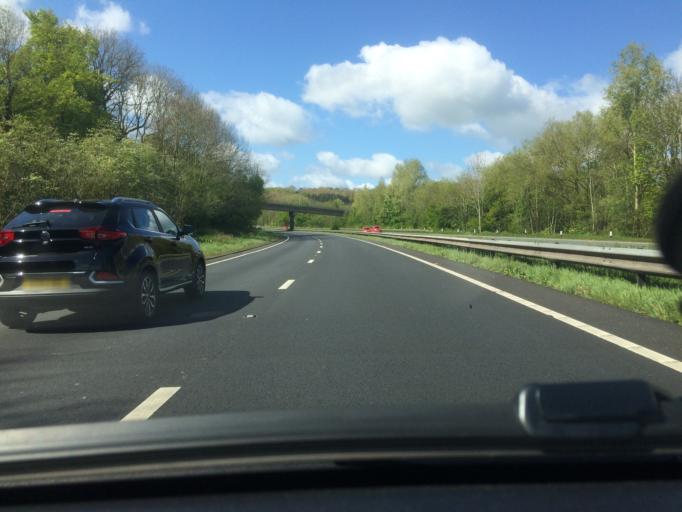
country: GB
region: Wales
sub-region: Wrexham
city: Gresford
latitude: 53.0902
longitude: -2.9808
